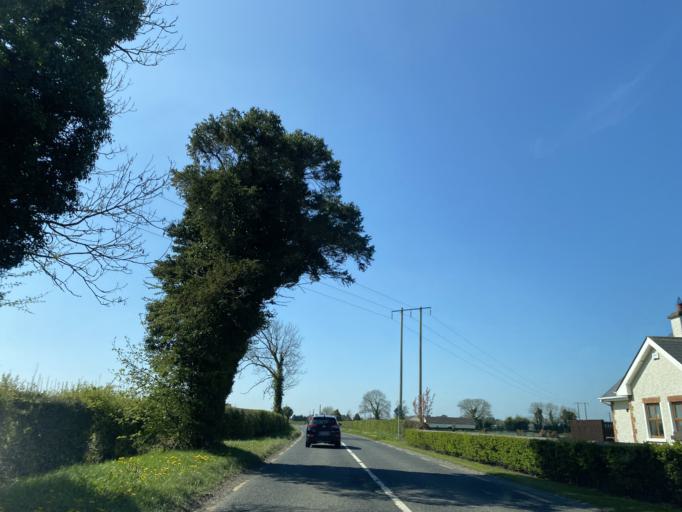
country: IE
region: Leinster
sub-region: Kildare
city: Kill
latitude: 53.2940
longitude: -6.6055
